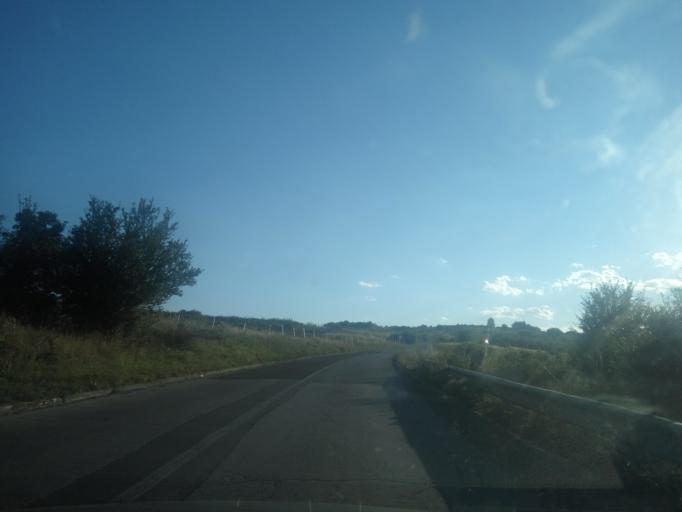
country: XK
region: Gjakova
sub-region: Komuna e Gjakoves
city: Gjakove
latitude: 42.4317
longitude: 20.4553
